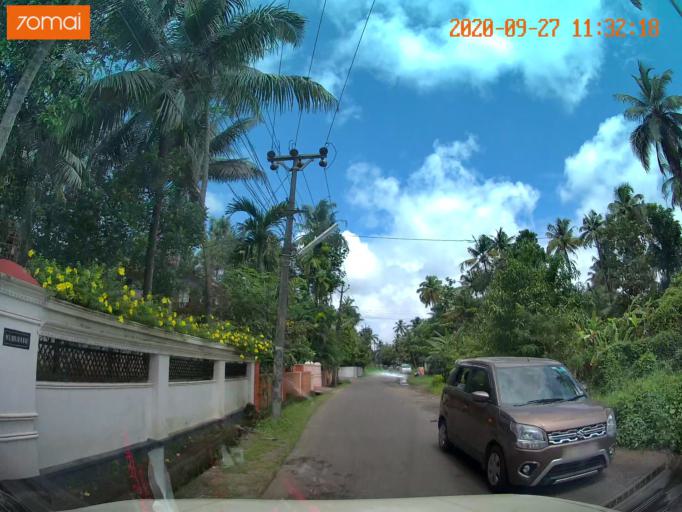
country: IN
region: Kerala
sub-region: Thrissur District
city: Thanniyam
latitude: 10.4265
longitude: 76.1307
